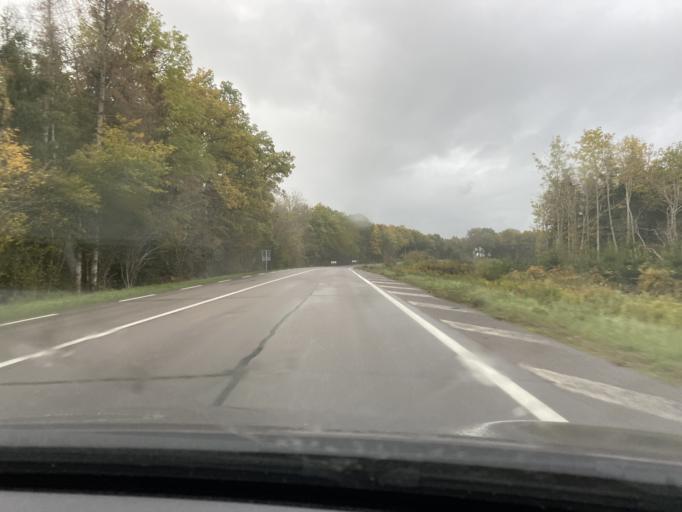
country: FR
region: Bourgogne
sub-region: Departement de la Cote-d'Or
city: Saulieu
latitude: 47.3326
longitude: 4.1928
